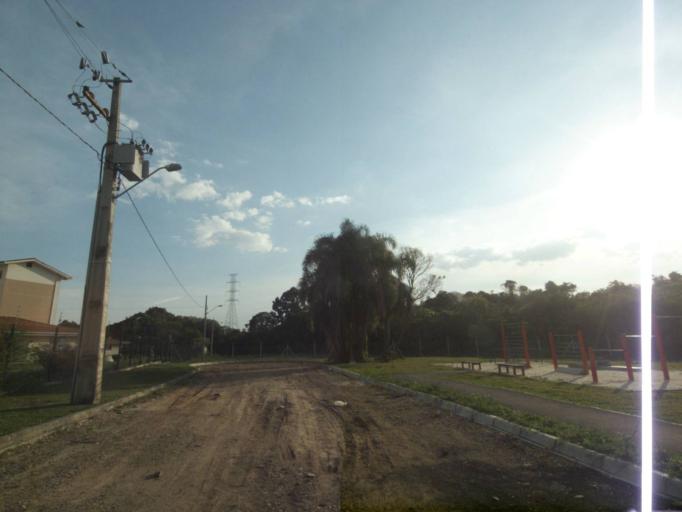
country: BR
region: Parana
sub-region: Curitiba
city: Curitiba
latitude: -25.4670
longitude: -49.3195
